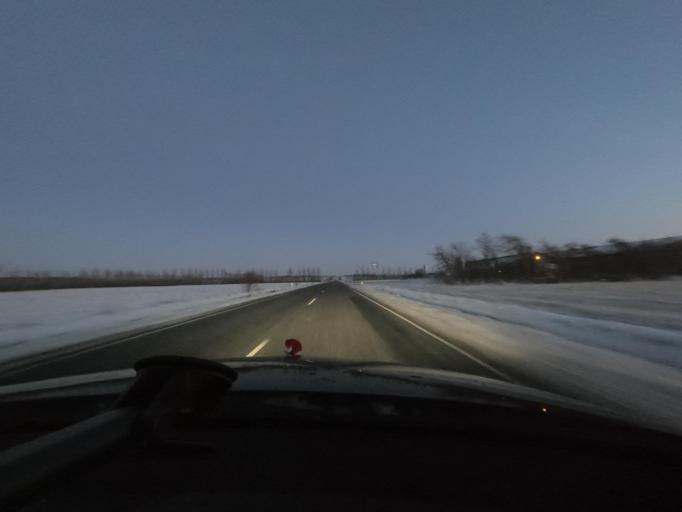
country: DK
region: South Denmark
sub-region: Tonder Kommune
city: Sherrebek
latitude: 55.1773
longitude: 8.8119
